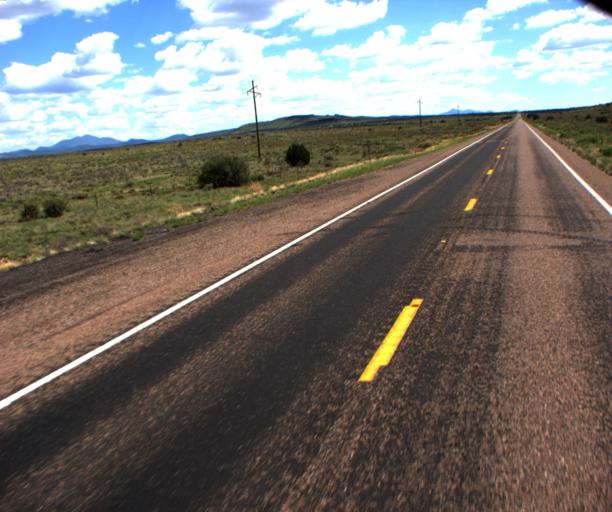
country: US
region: Arizona
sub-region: Coconino County
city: Williams
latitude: 35.5815
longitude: -112.1522
